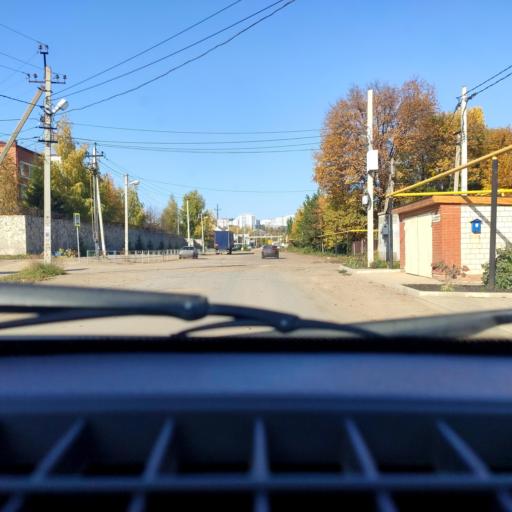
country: RU
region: Bashkortostan
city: Ufa
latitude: 54.7022
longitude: 55.9546
